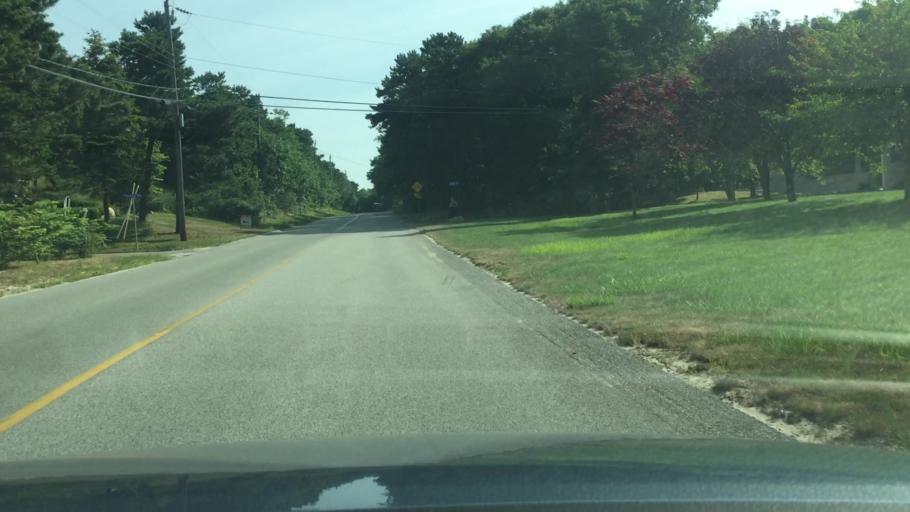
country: US
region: Massachusetts
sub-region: Barnstable County
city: Truro
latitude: 42.0230
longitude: -70.0713
